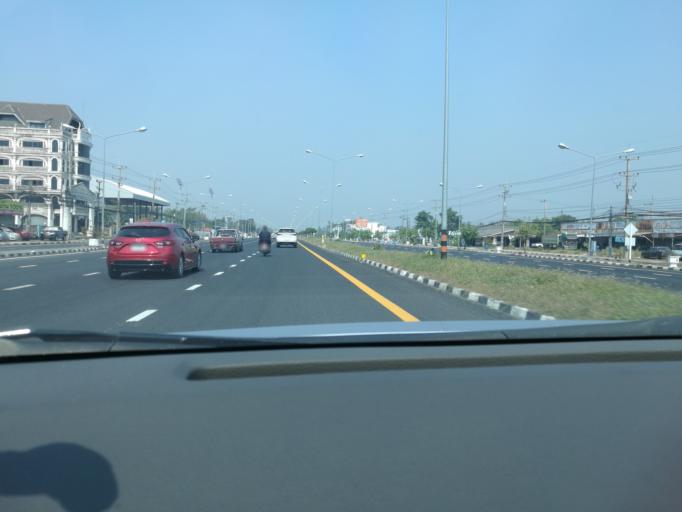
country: TH
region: Sara Buri
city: Saraburi
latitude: 14.5537
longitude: 100.9068
